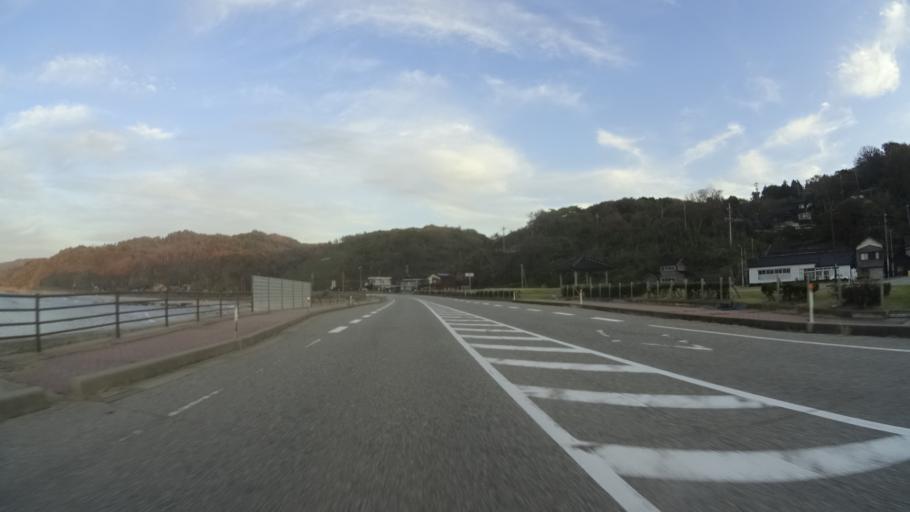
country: JP
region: Ishikawa
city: Nanao
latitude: 37.2485
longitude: 136.7098
